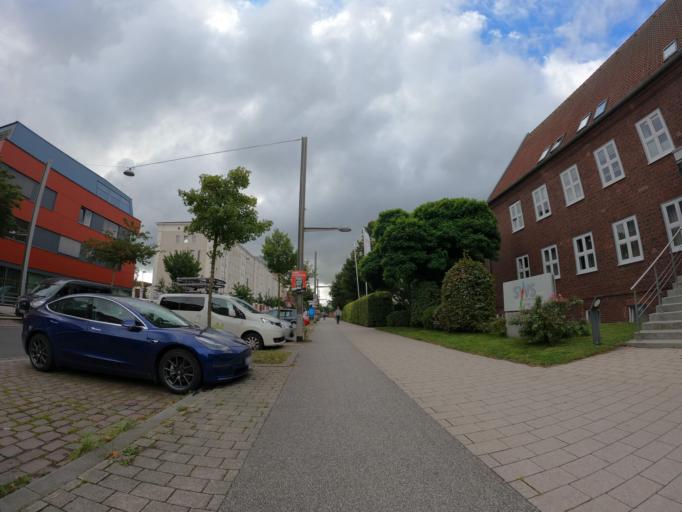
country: DE
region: Mecklenburg-Vorpommern
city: Stralsund
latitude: 54.3113
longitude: 13.0971
